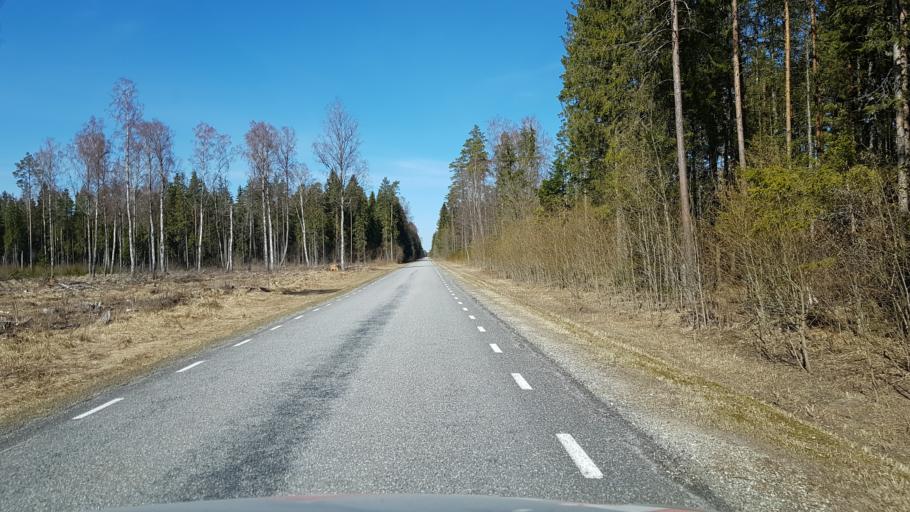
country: EE
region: Laeaene-Virumaa
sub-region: Vinni vald
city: Vinni
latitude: 59.1464
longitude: 26.5212
